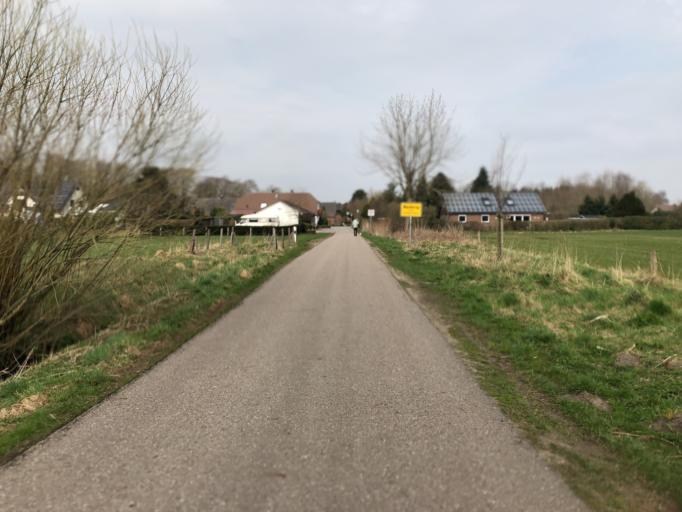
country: DE
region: Schleswig-Holstein
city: Wanderup
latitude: 54.6856
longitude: 9.3374
